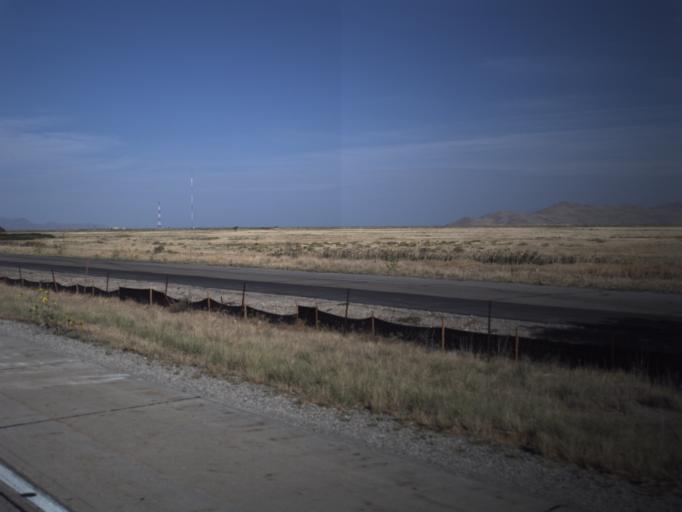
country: US
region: Utah
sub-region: Salt Lake County
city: Magna
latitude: 40.7711
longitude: -112.0749
